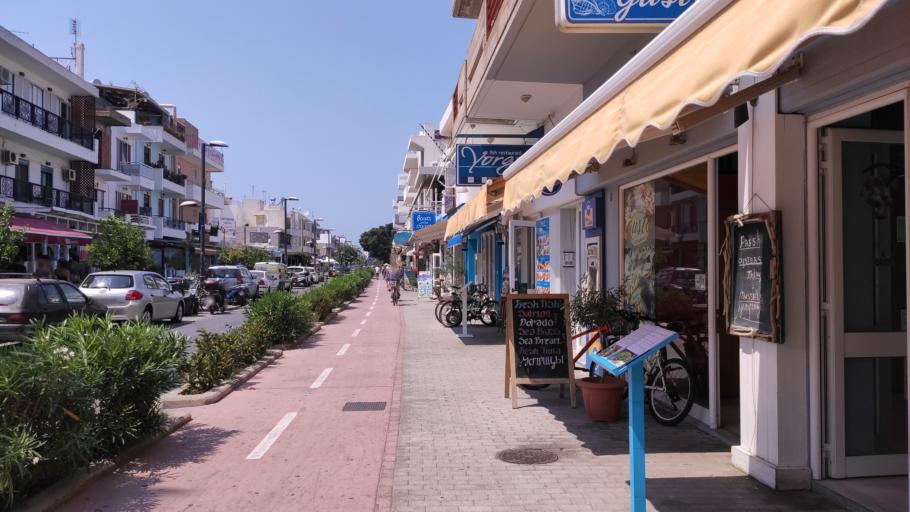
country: GR
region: South Aegean
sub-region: Nomos Dodekanisou
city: Kos
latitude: 36.8980
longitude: 27.2870
